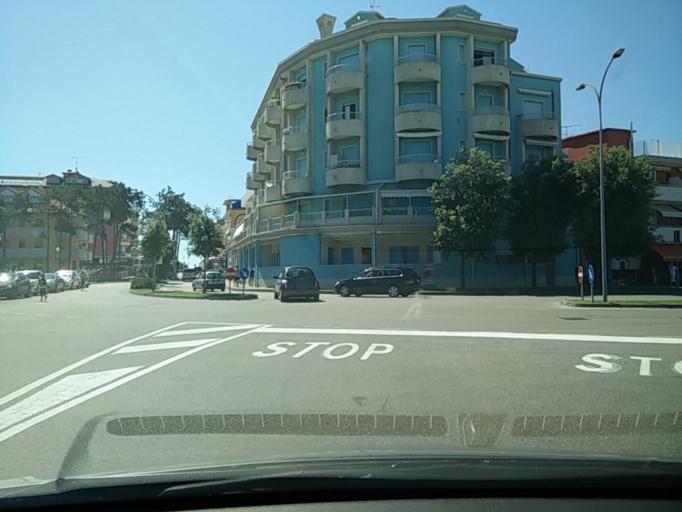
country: IT
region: Veneto
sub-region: Provincia di Venezia
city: Caorle
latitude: 45.6091
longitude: 12.8937
